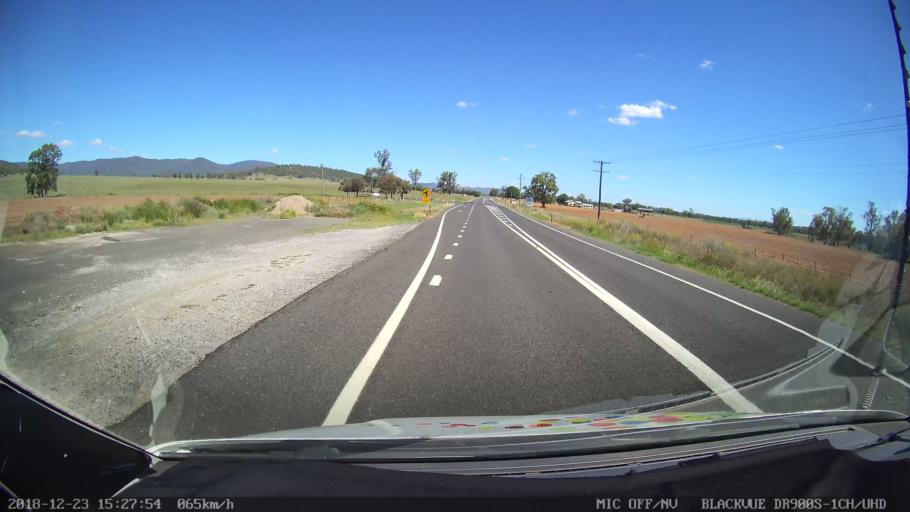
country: AU
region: New South Wales
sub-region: Tamworth Municipality
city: East Tamworth
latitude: -30.9313
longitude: 150.8483
